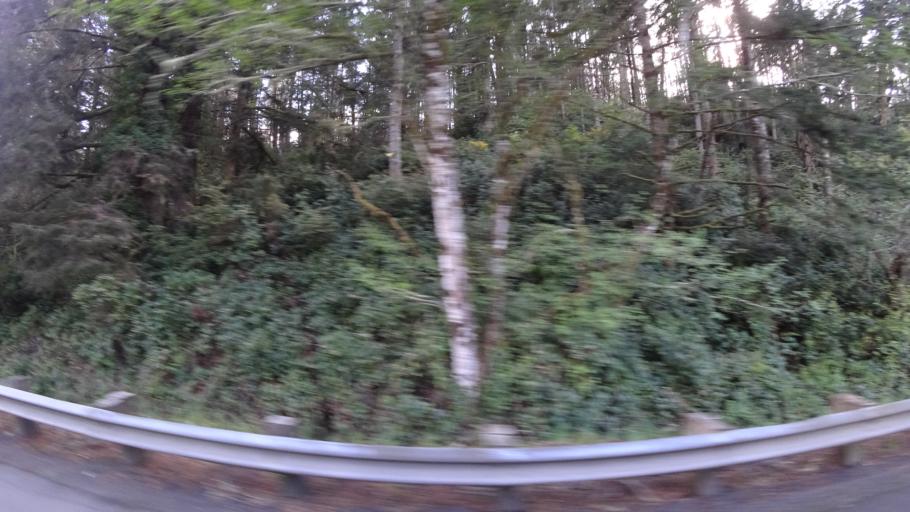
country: US
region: Oregon
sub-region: Lane County
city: Dunes City
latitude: 43.8066
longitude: -124.1520
